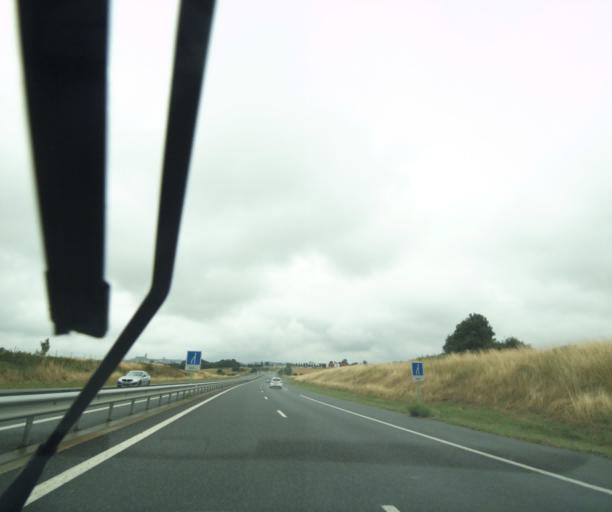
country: FR
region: Midi-Pyrenees
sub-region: Departement de l'Aveyron
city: Luc-la-Primaube
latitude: 44.3209
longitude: 2.5504
